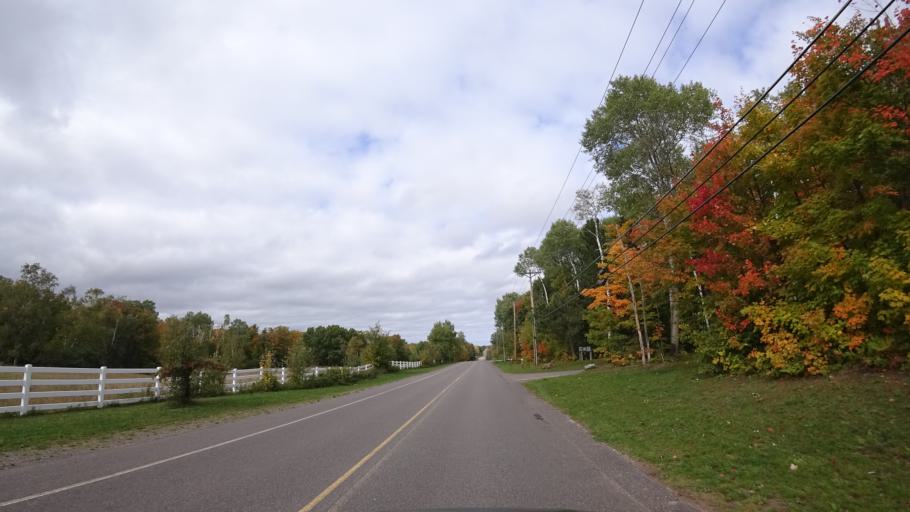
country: US
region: Michigan
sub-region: Marquette County
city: Trowbridge Park
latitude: 46.5398
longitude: -87.4374
